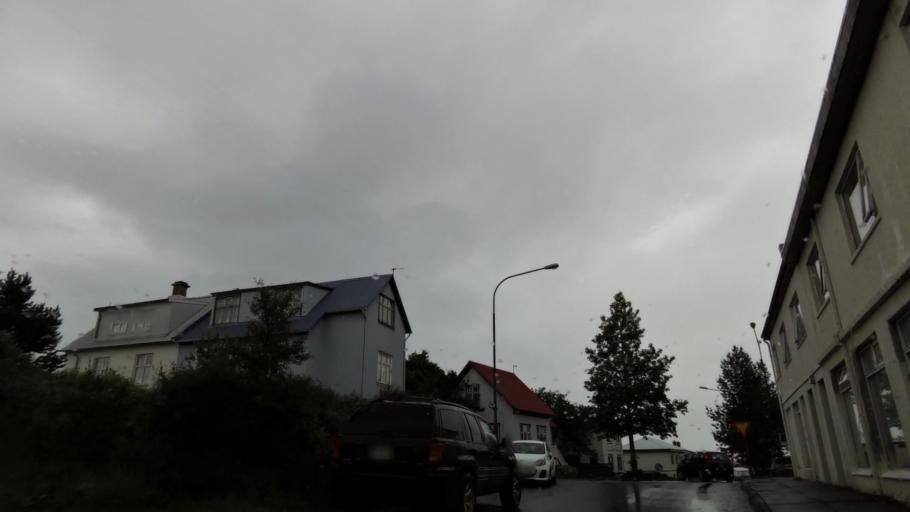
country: IS
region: Capital Region
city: Hafnarfjoerdur
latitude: 64.0715
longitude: -21.9607
